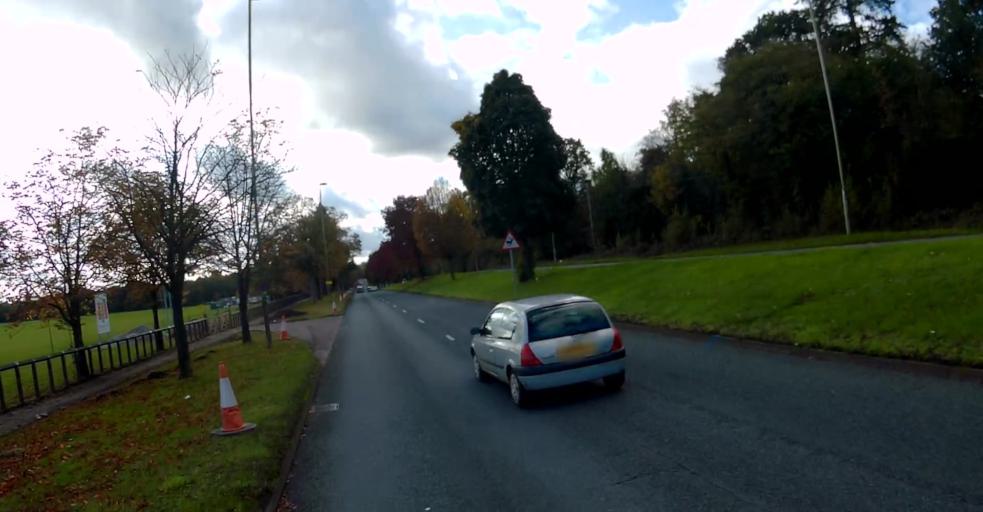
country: GB
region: England
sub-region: Hampshire
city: Aldershot
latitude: 51.2685
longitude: -0.7608
